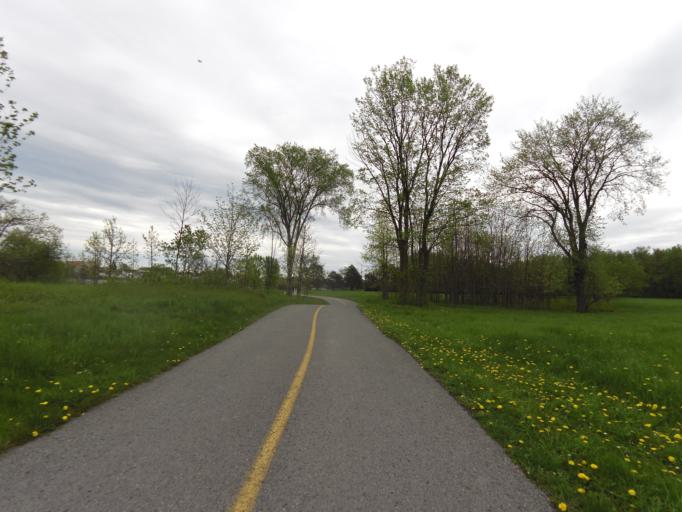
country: CA
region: Quebec
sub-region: Outaouais
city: Gatineau
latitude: 45.4571
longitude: -75.7087
